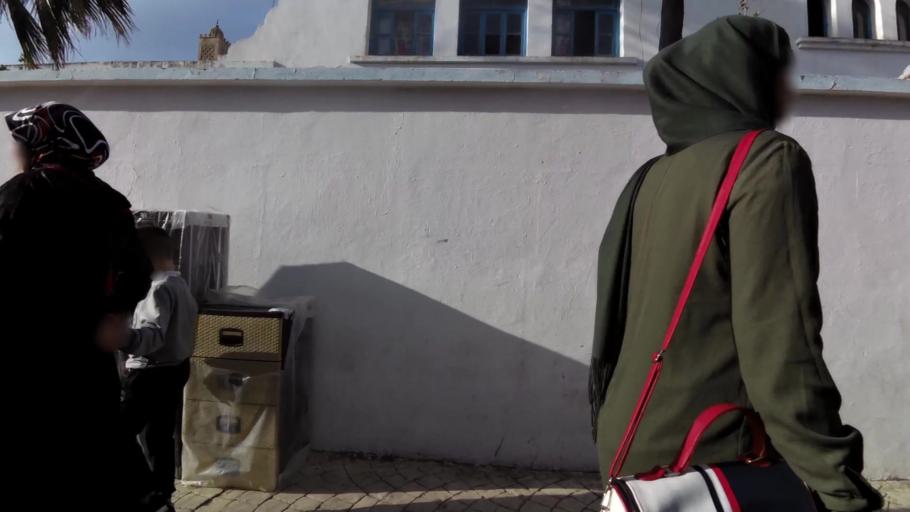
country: MA
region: Tanger-Tetouan
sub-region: Tetouan
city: Martil
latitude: 35.6168
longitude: -5.2754
